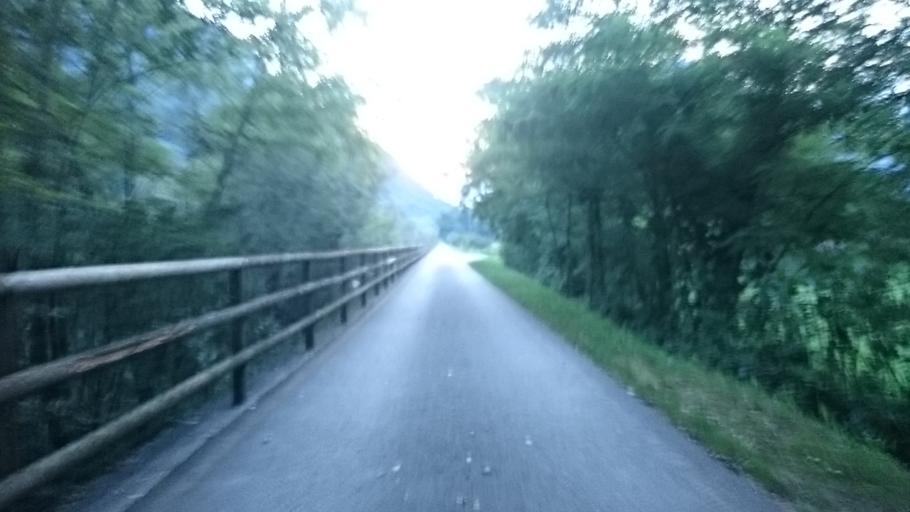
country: IT
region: Trentino-Alto Adige
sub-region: Provincia di Trento
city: Grigno
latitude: 45.9994
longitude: 11.6564
